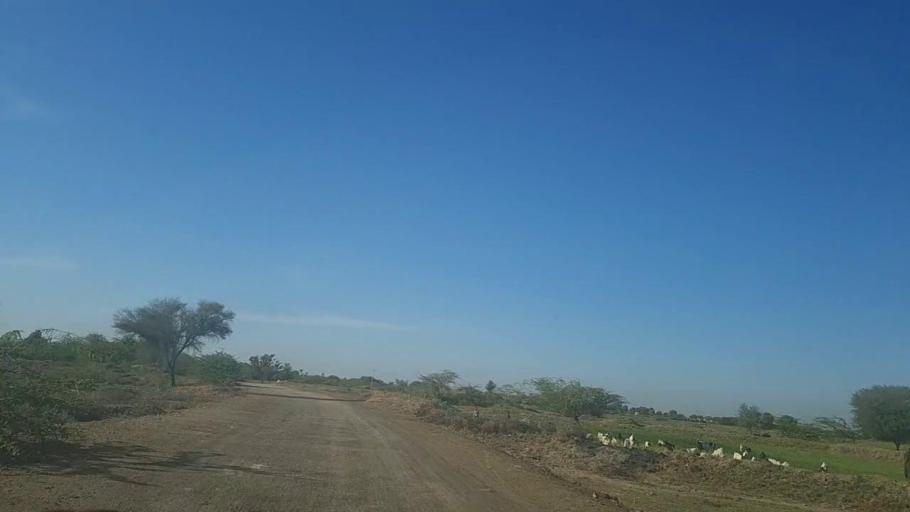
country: PK
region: Sindh
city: Pithoro
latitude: 25.5206
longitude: 69.3822
